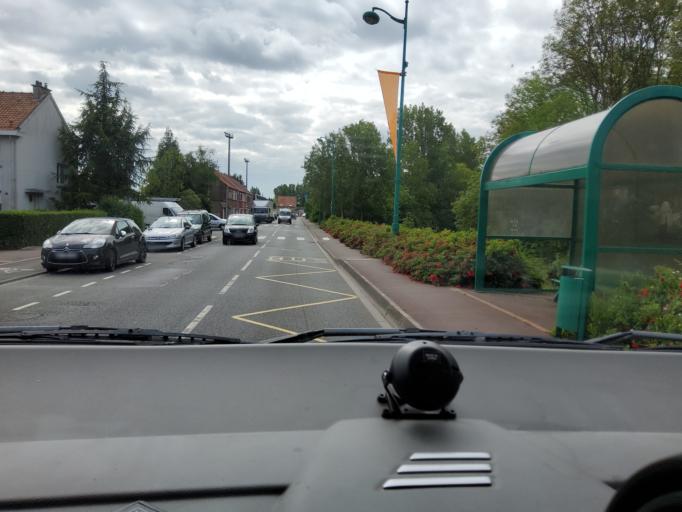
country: FR
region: Nord-Pas-de-Calais
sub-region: Departement du Nord
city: Gravelines
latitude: 50.9918
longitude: 2.1318
